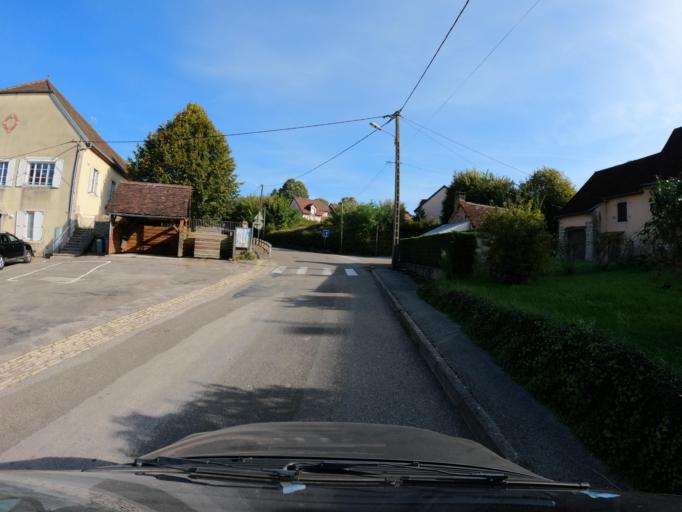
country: FR
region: Franche-Comte
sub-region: Departement du Jura
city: Montmorot
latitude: 46.6860
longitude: 5.5377
